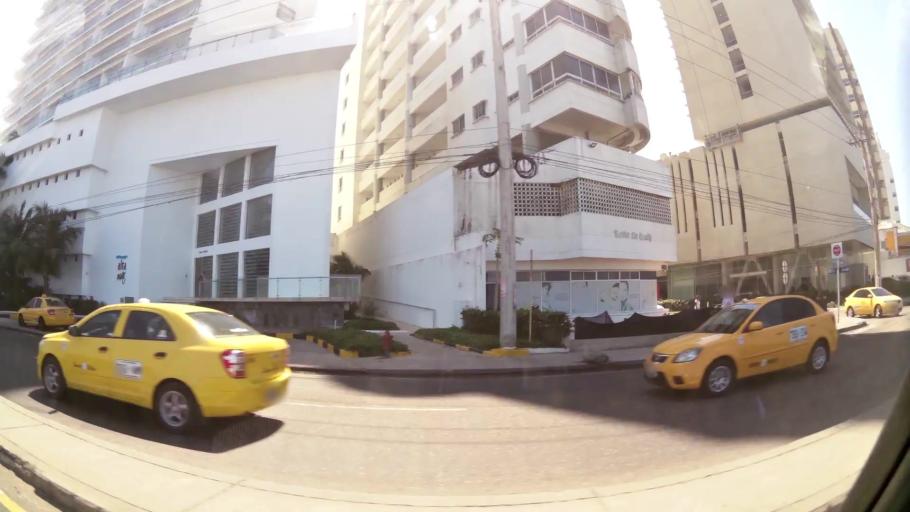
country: CO
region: Bolivar
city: Cartagena
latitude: 10.4370
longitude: -75.5354
